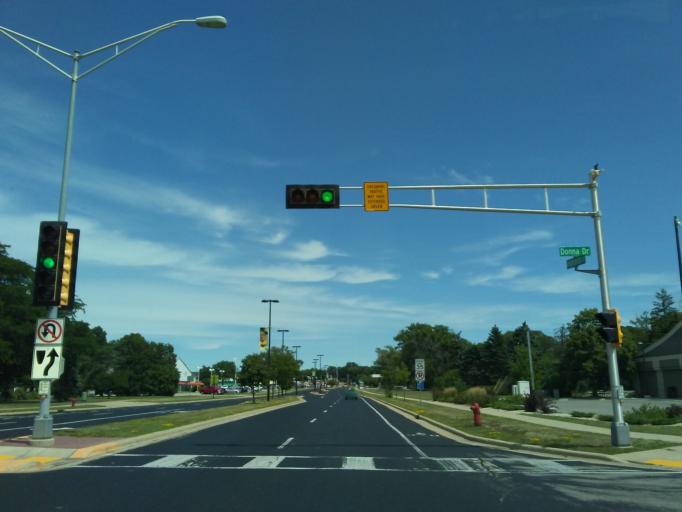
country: US
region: Wisconsin
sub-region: Dane County
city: Middleton
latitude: 43.1060
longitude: -89.5106
